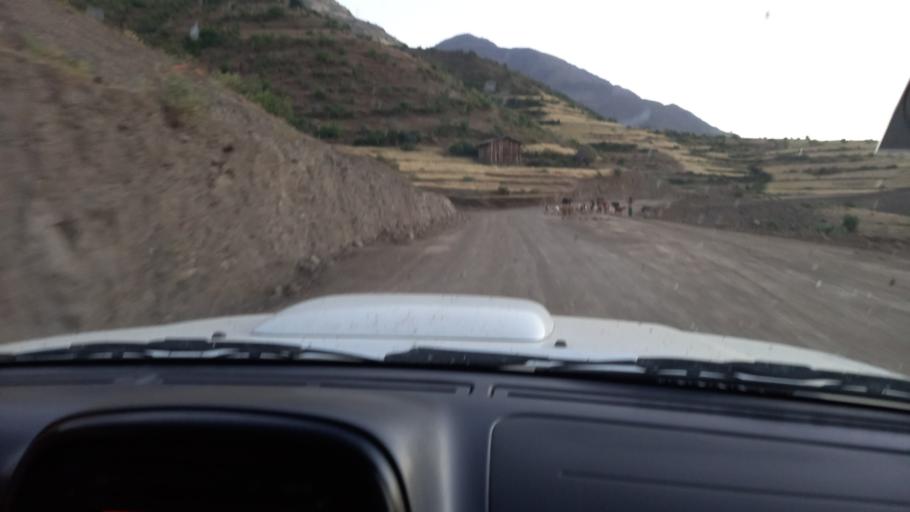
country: ET
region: Amhara
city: Debark'
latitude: 13.0363
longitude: 38.0556
